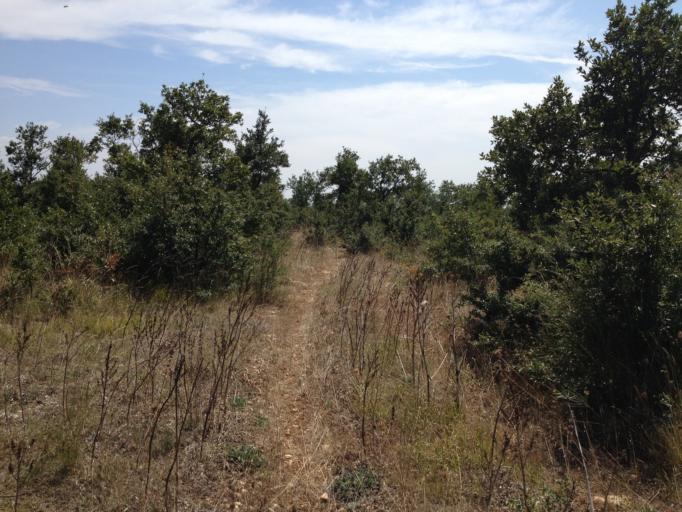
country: IT
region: Apulia
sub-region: Provincia di Bari
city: Gioia del Colle
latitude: 40.8267
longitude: 16.9907
